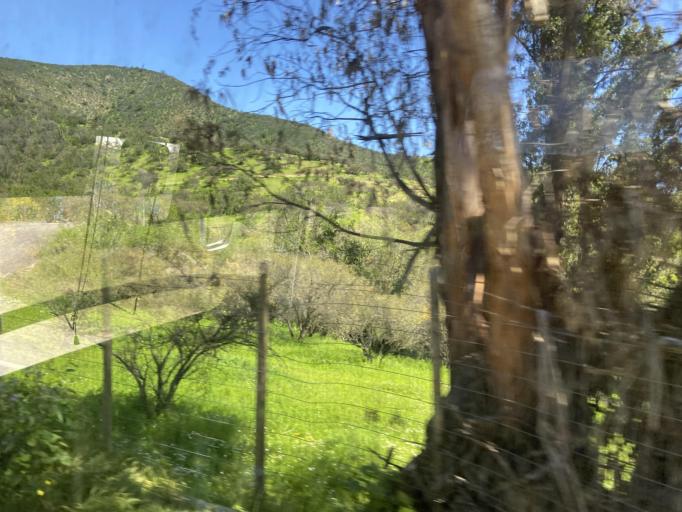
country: CL
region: Valparaiso
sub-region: Provincia de Marga Marga
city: Villa Alemana
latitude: -33.1724
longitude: -71.3140
